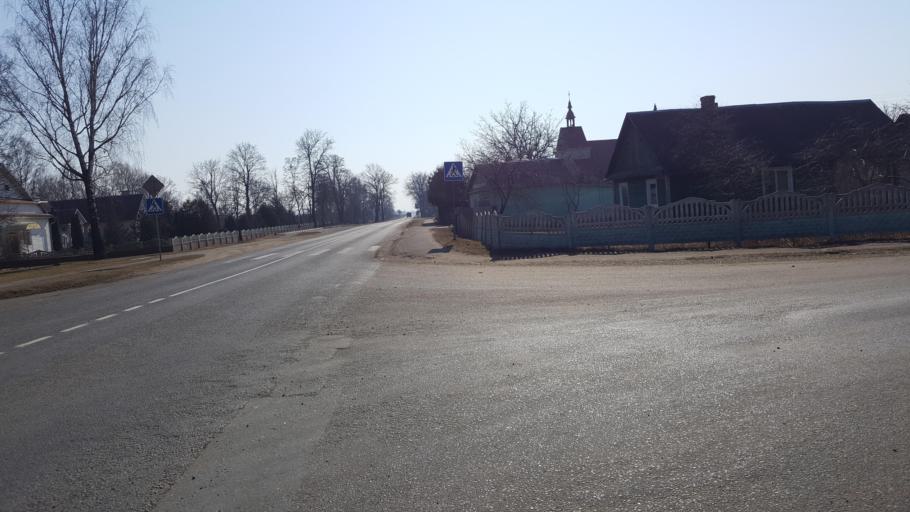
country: BY
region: Brest
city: Kamyanyets
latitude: 52.3169
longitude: 23.9198
